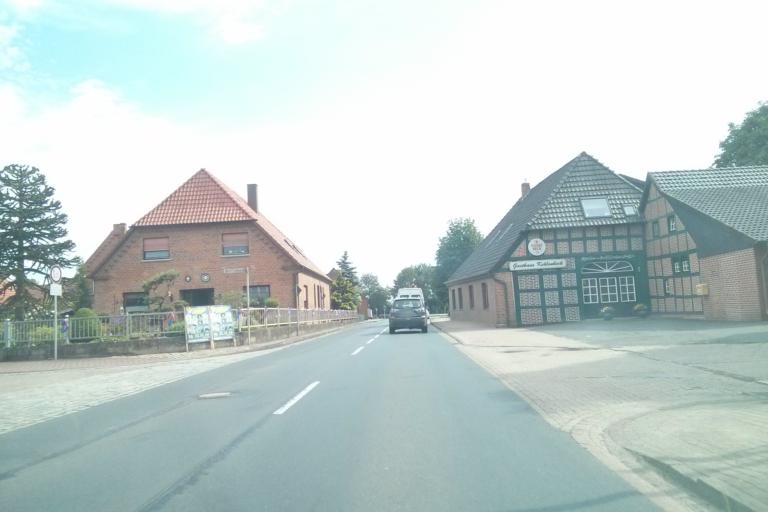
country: DE
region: Lower Saxony
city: Ahsen-Oetzen
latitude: 52.9678
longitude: 9.0492
